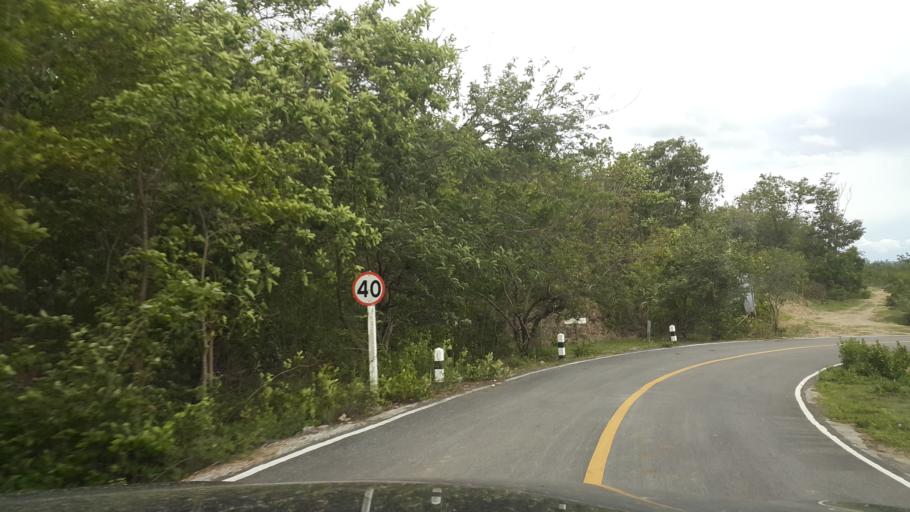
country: TH
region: Sukhothai
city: Thung Saliam
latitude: 17.1801
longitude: 99.4831
